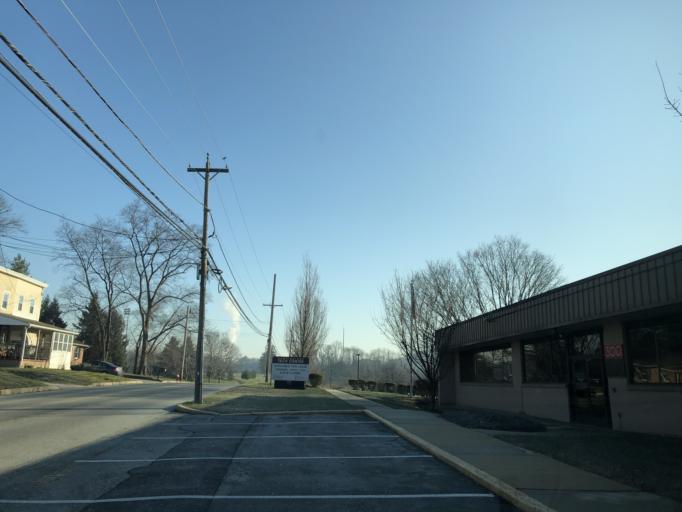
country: US
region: Pennsylvania
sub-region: Chester County
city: Downingtown
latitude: 40.0059
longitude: -75.6897
